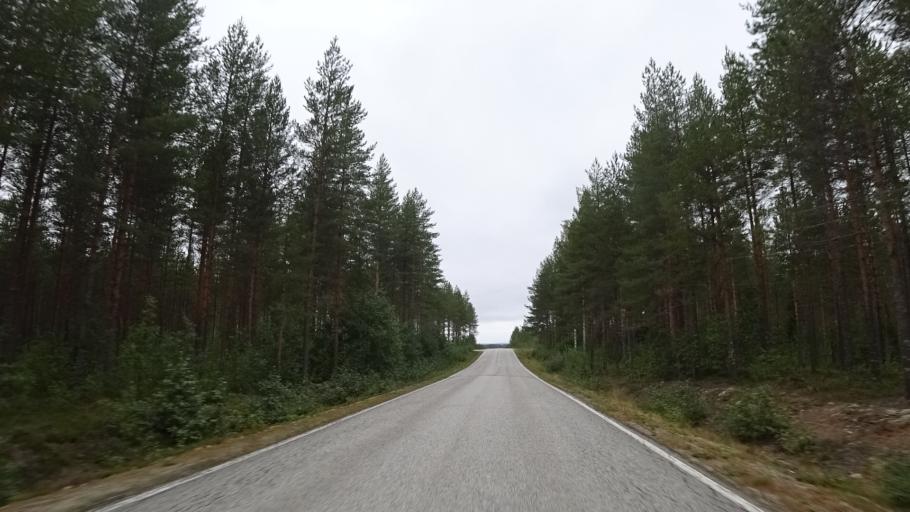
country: FI
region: North Karelia
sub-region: Pielisen Karjala
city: Lieksa
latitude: 63.3626
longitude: 30.2821
